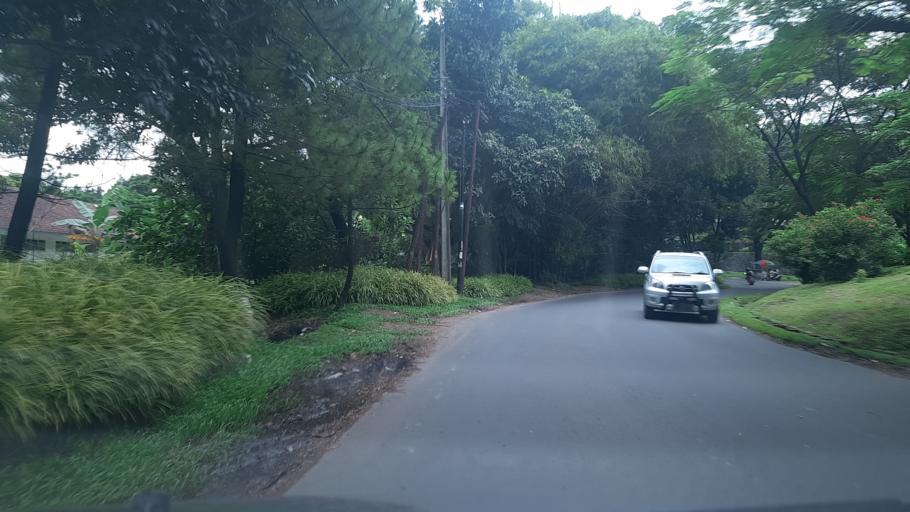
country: ID
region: West Java
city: Bogor
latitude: -6.5730
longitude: 106.8644
